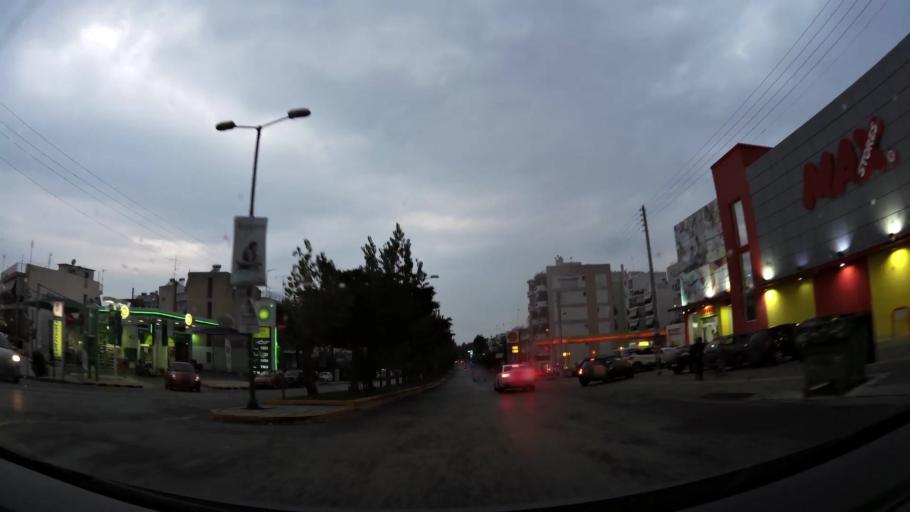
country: GR
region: Attica
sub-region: Nomarchia Athinas
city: Ymittos
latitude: 37.9436
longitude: 23.7485
